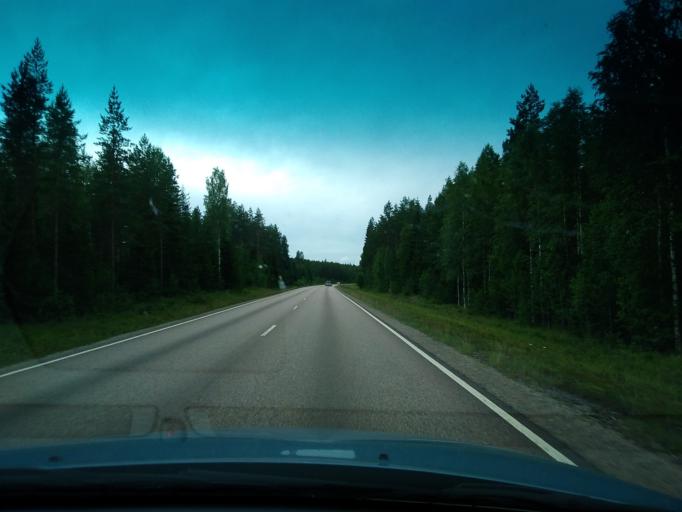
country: FI
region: Central Finland
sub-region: Keuruu
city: Multia
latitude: 62.3839
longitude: 24.7537
